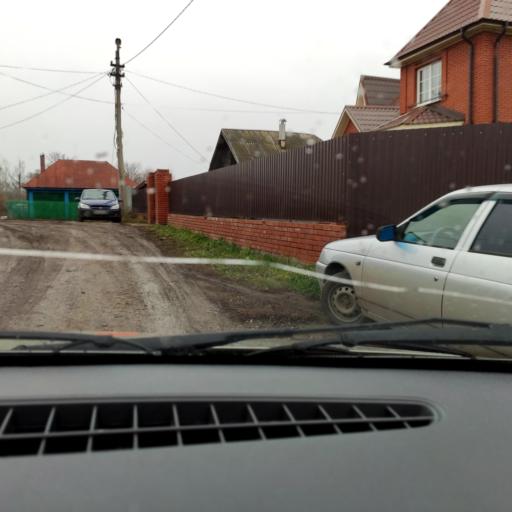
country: RU
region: Bashkortostan
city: Ufa
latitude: 54.6087
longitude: 55.9475
